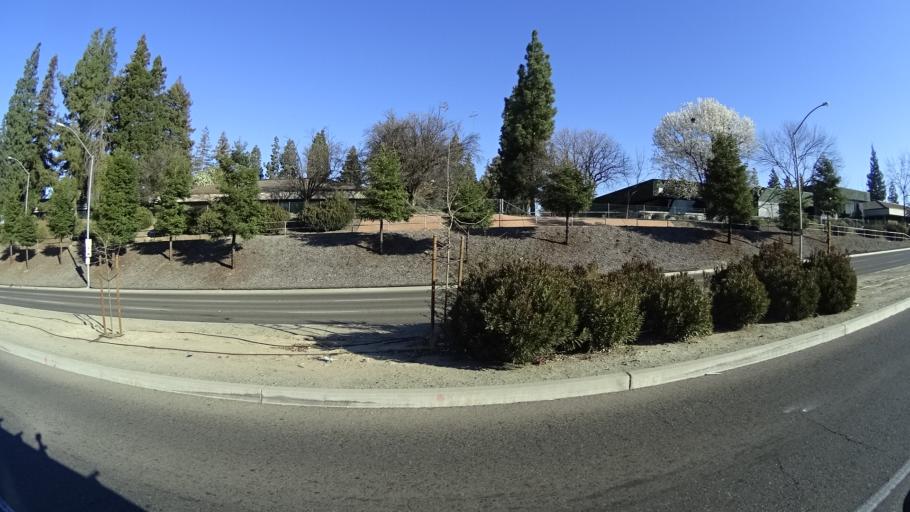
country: US
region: California
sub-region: Fresno County
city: Fresno
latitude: 36.8081
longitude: -119.8402
